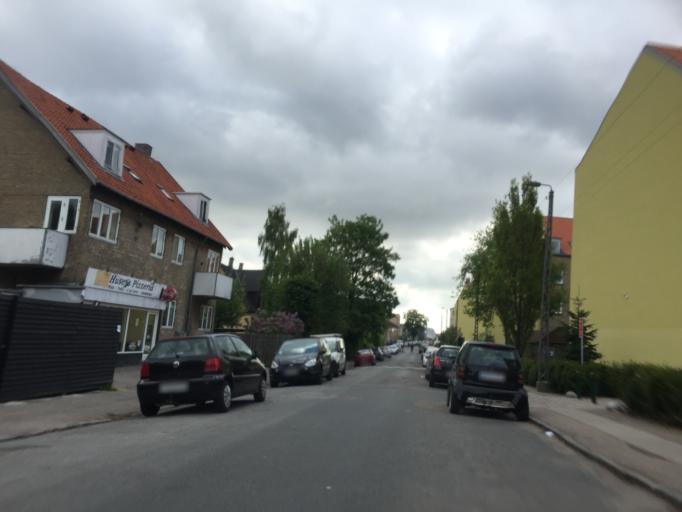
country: DK
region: Capital Region
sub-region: Frederiksberg Kommune
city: Frederiksberg
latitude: 55.7091
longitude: 12.5190
